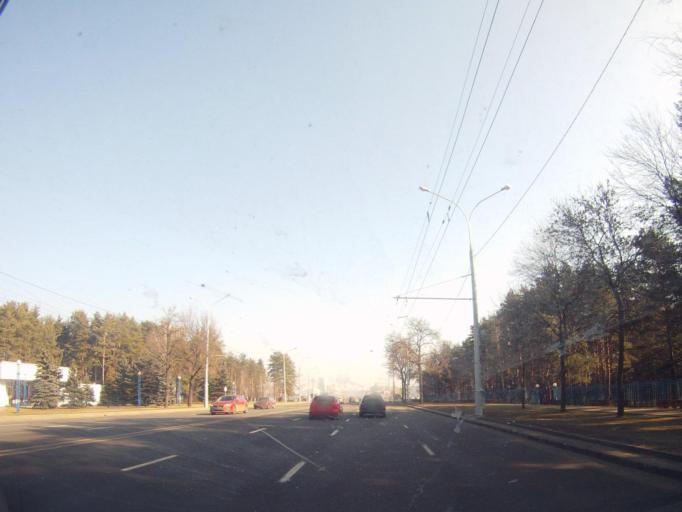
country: BY
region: Minsk
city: Borovlyany
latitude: 53.9374
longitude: 27.6622
